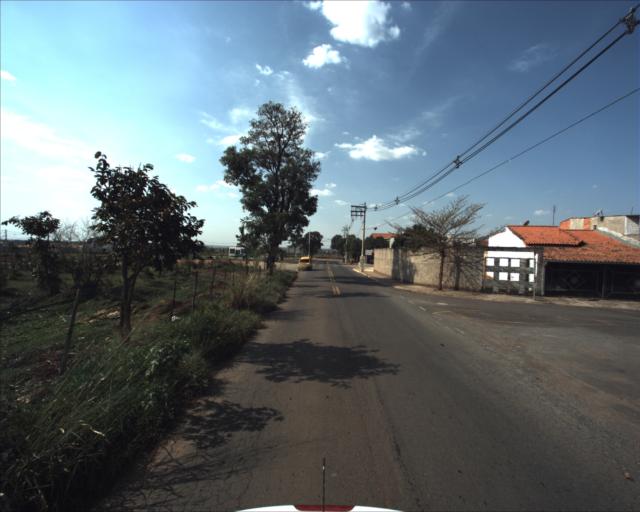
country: BR
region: Sao Paulo
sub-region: Sorocaba
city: Sorocaba
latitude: -23.4950
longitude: -47.5325
